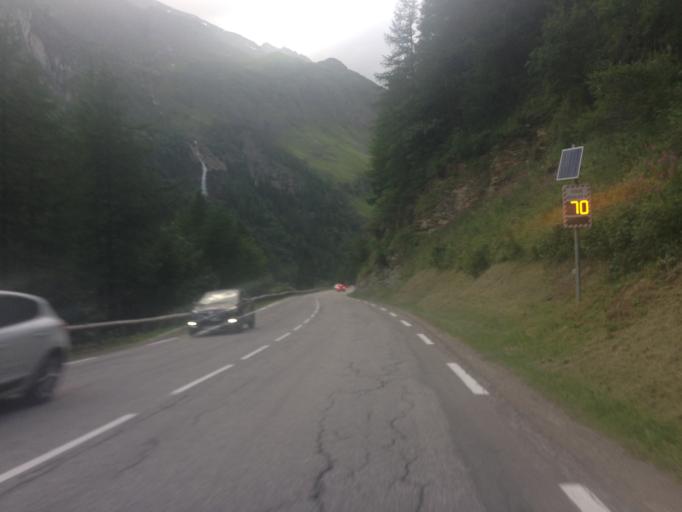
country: FR
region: Rhone-Alpes
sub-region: Departement de la Savoie
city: Tignes
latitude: 45.5127
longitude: 6.9192
